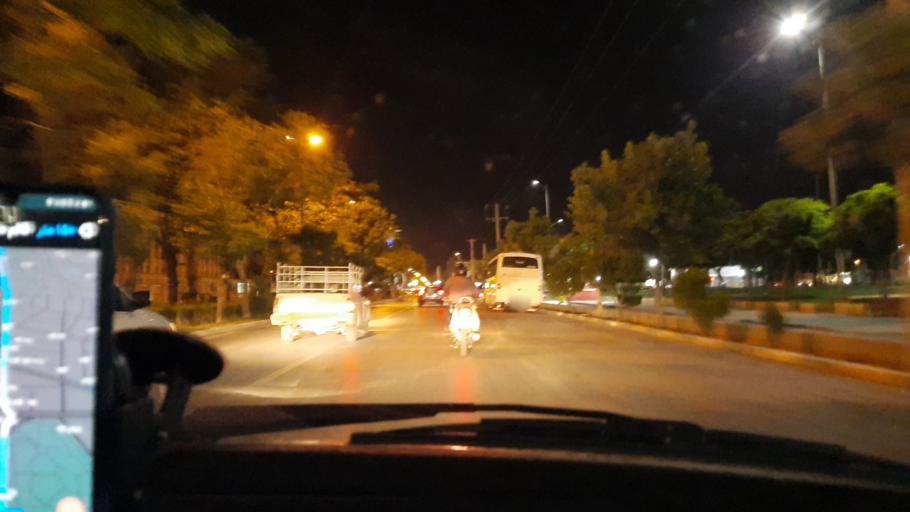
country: IR
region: Markazi
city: Arak
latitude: 34.1062
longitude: 49.6964
